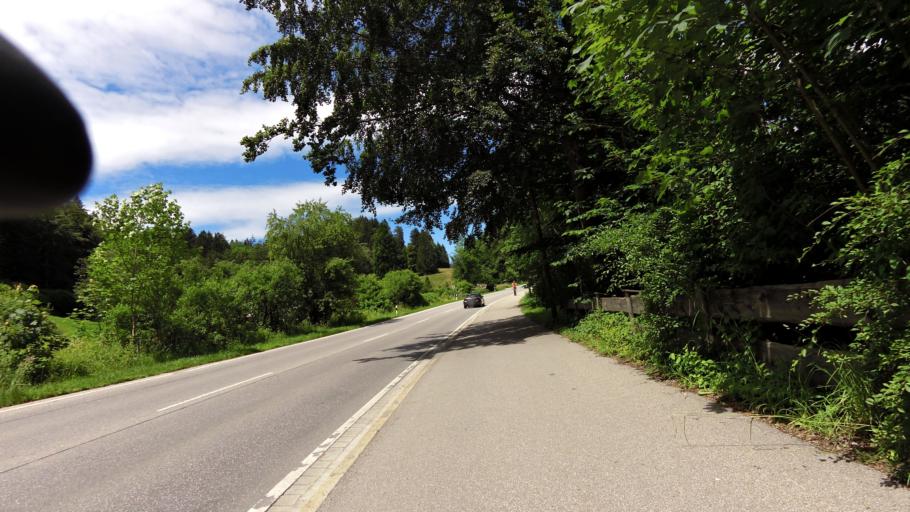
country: DE
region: Bavaria
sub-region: Upper Bavaria
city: Bad Wiessee
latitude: 47.6954
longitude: 11.7327
